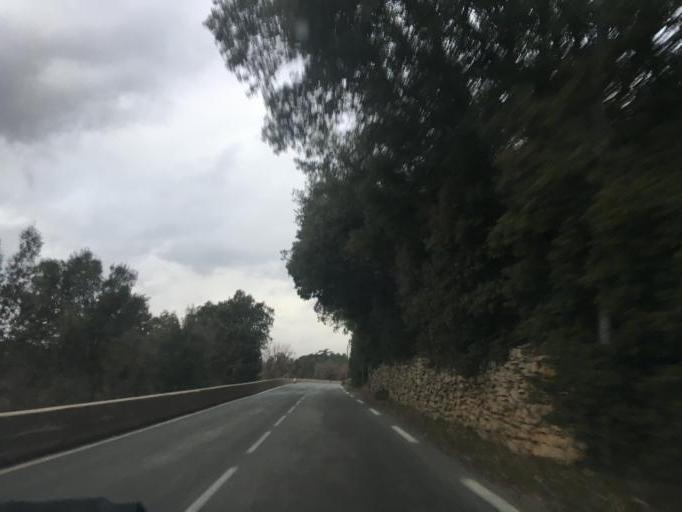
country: FR
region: Provence-Alpes-Cote d'Azur
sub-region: Departement du Var
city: Besse-sur-Issole
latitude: 43.3388
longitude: 6.1605
